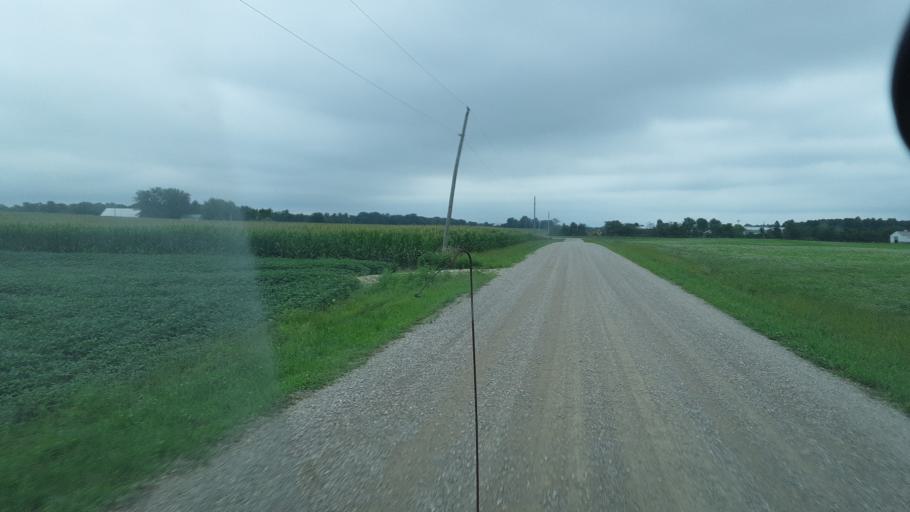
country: US
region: Indiana
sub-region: Adams County
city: Geneva
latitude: 40.6203
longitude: -84.9976
